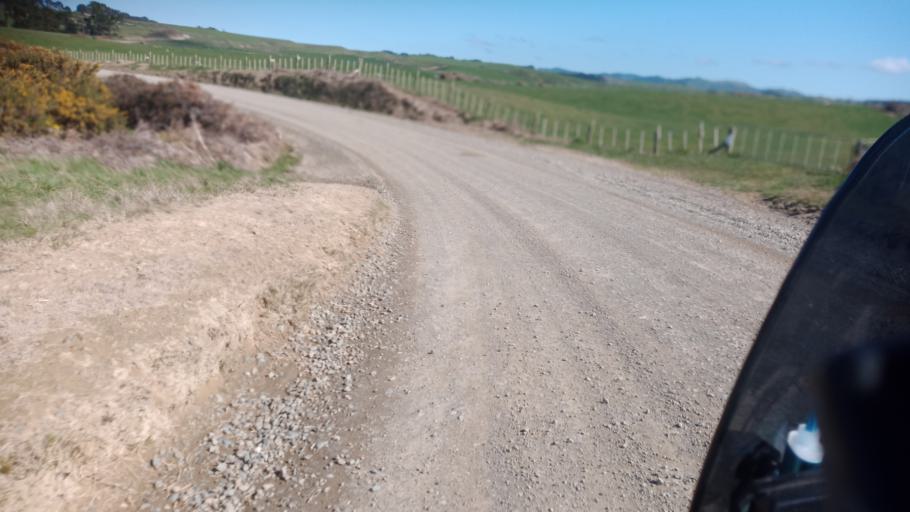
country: NZ
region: Gisborne
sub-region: Gisborne District
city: Gisborne
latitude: -39.1053
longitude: 177.9624
